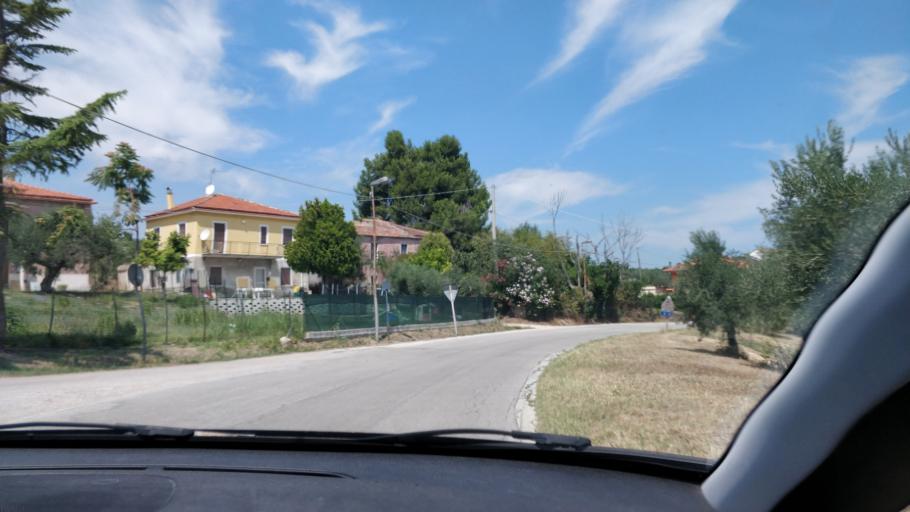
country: IT
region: Abruzzo
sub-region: Provincia di Chieti
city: Torrevecchia
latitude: 42.3931
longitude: 14.1988
